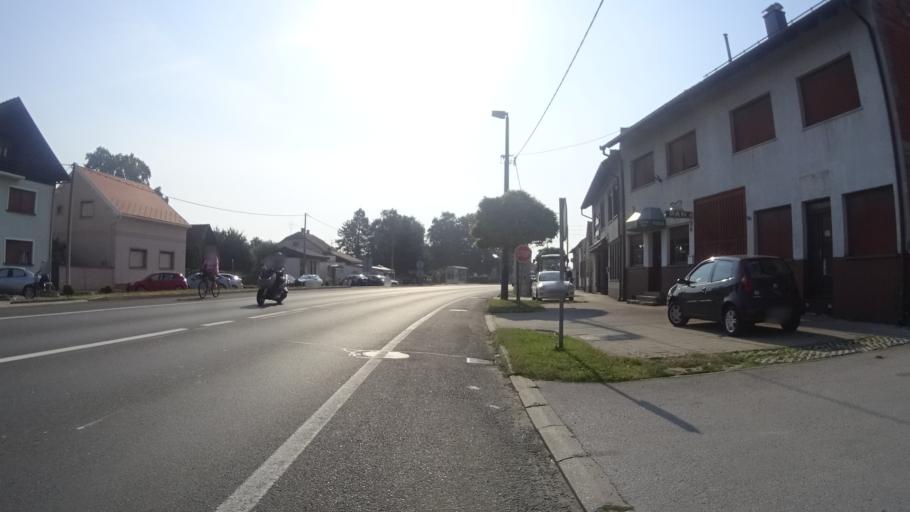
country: HR
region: Medimurska
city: Nedelisce
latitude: 46.3767
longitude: 16.3838
